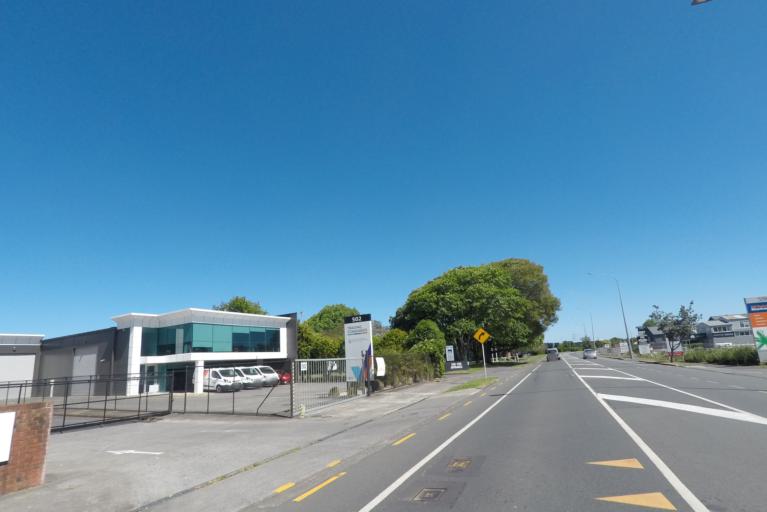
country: NZ
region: Auckland
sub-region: Auckland
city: Rosebank
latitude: -36.8790
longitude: 174.6712
